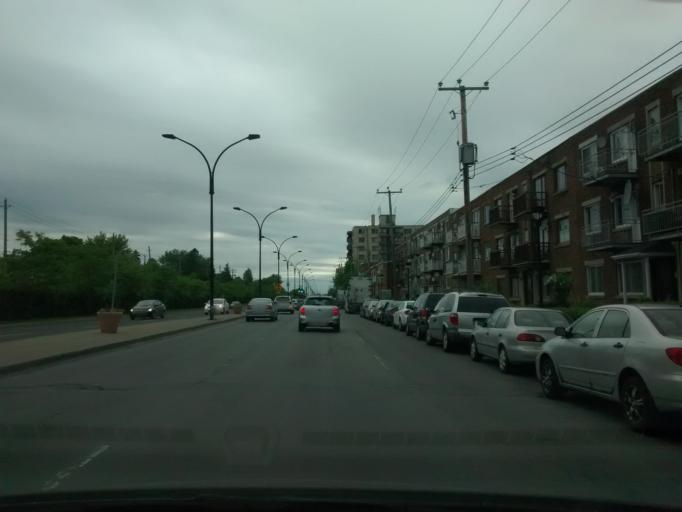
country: CA
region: Quebec
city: Mont-Royal
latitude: 45.5279
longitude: -73.6385
